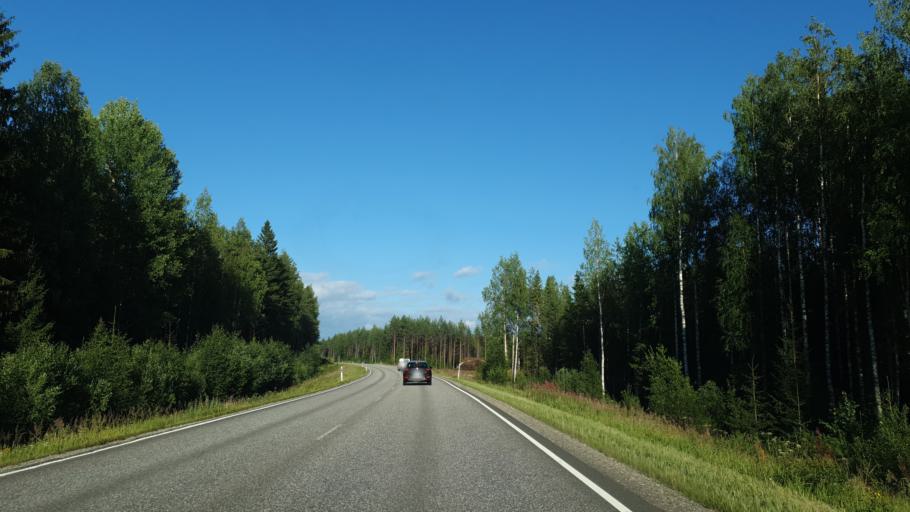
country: FI
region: North Karelia
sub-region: Joensuu
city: Outokumpu
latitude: 62.5197
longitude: 29.0177
